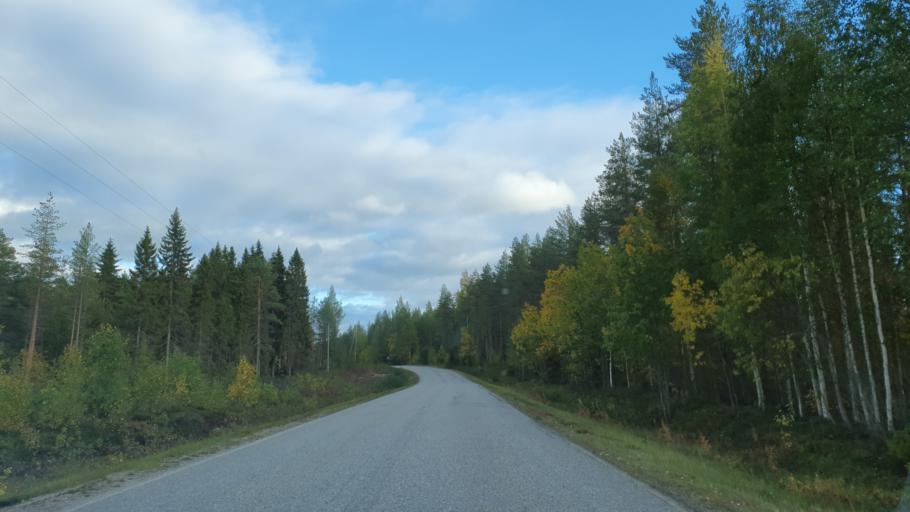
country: FI
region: Kainuu
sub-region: Kehys-Kainuu
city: Kuhmo
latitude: 63.9304
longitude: 29.9942
